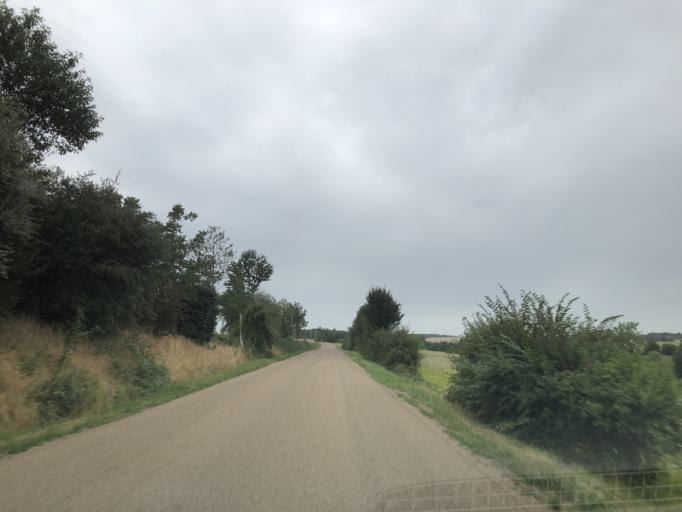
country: FR
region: Bourgogne
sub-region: Departement de l'Yonne
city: Charny
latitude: 47.9545
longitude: 3.1360
